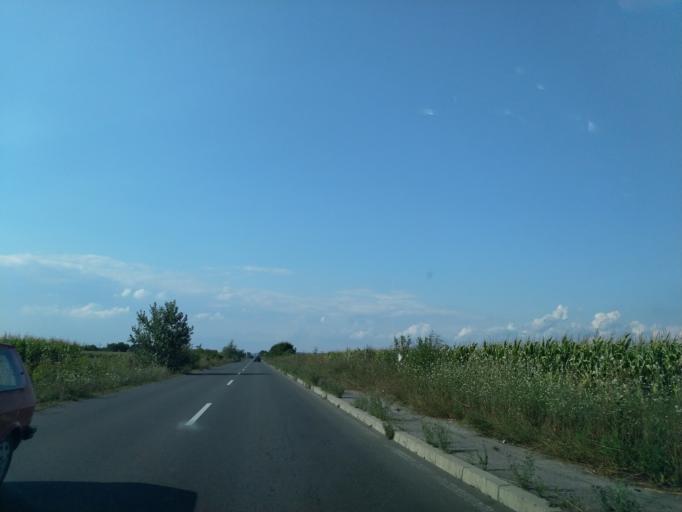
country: RS
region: Central Serbia
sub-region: Pomoravski Okrug
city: Paracin
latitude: 43.8212
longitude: 21.4185
